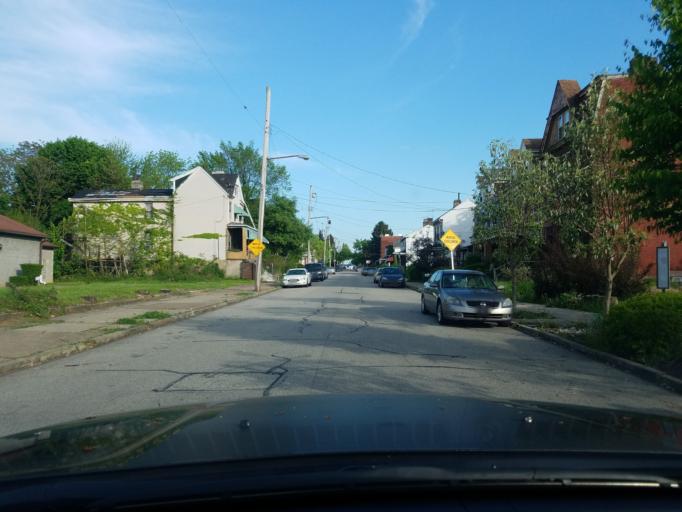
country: US
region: Pennsylvania
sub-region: Allegheny County
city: Aspinwall
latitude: 40.4642
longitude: -79.9163
